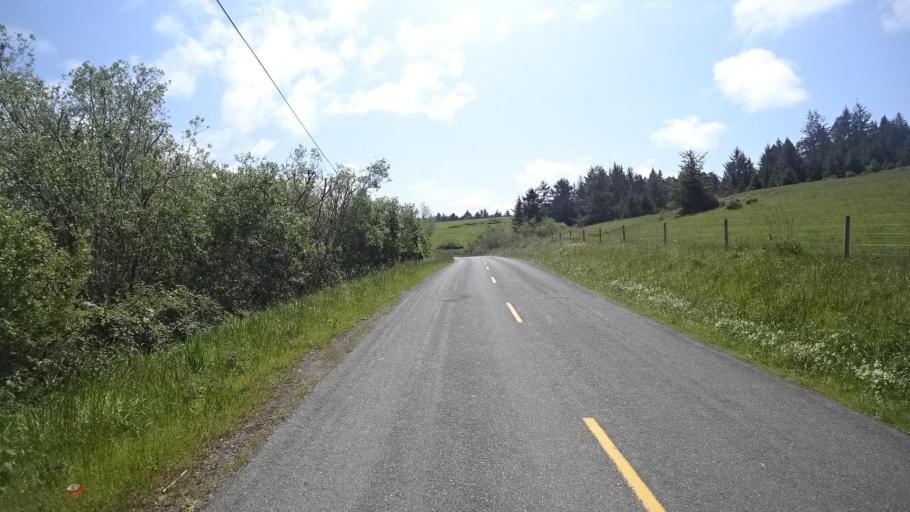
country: US
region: California
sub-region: Humboldt County
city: Humboldt Hill
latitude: 40.6699
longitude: -124.2088
